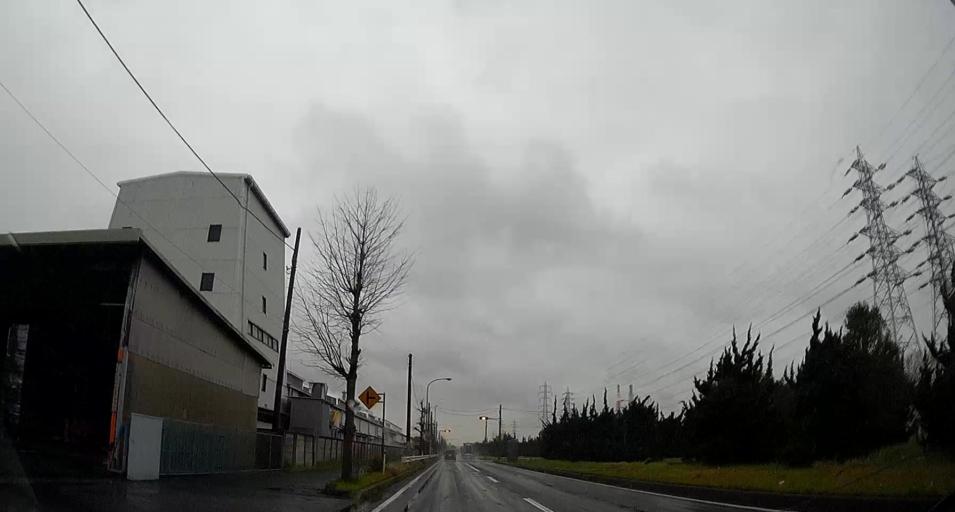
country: JP
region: Chiba
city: Ichihara
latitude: 35.4948
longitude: 140.0458
